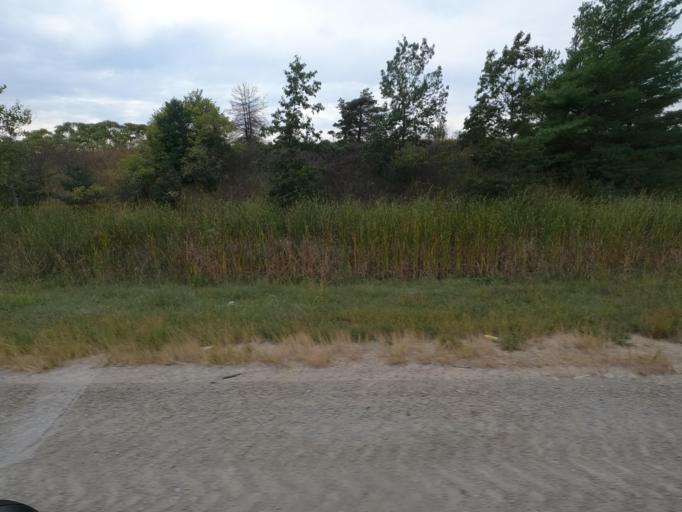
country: US
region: Iowa
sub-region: Marion County
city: Pella
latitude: 41.4093
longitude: -92.9463
